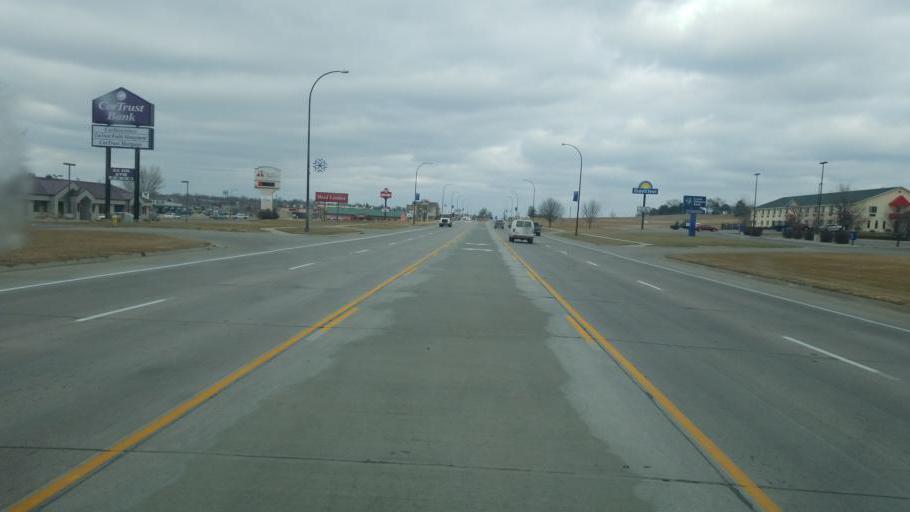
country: US
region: South Dakota
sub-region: Yankton County
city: Yankton
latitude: 42.8960
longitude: -97.3975
